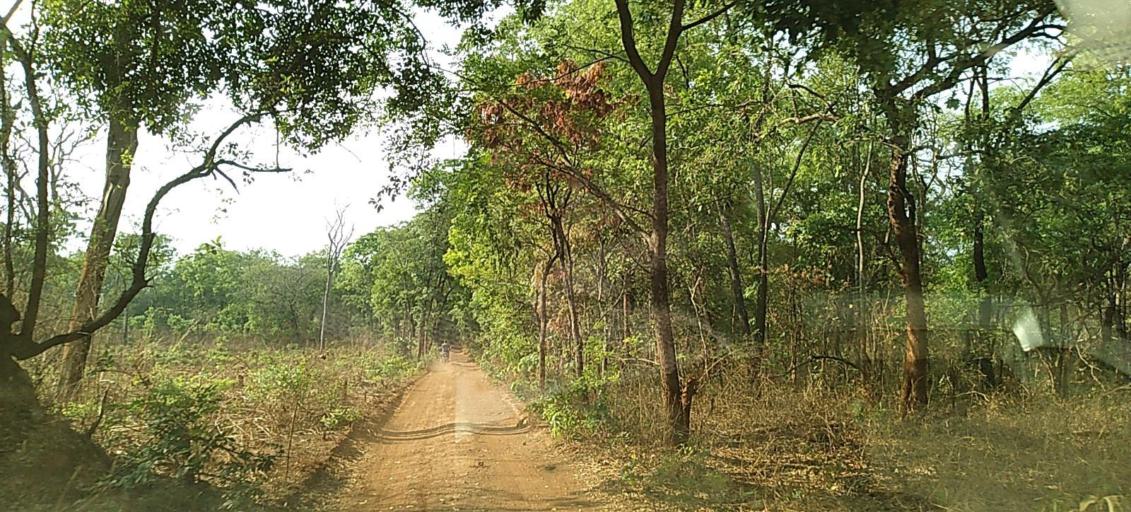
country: ZM
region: Copperbelt
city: Kalulushi
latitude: -12.9699
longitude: 27.7142
